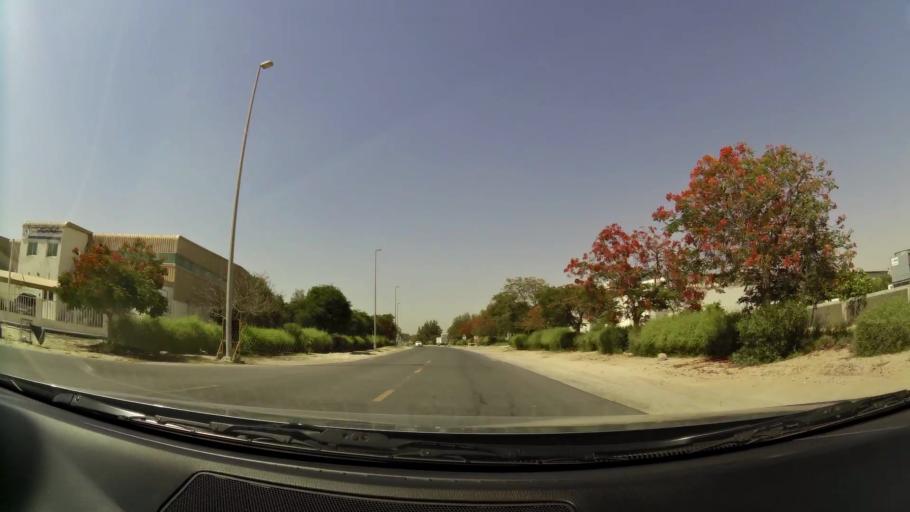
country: AE
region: Dubai
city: Dubai
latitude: 24.9817
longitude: 55.1482
